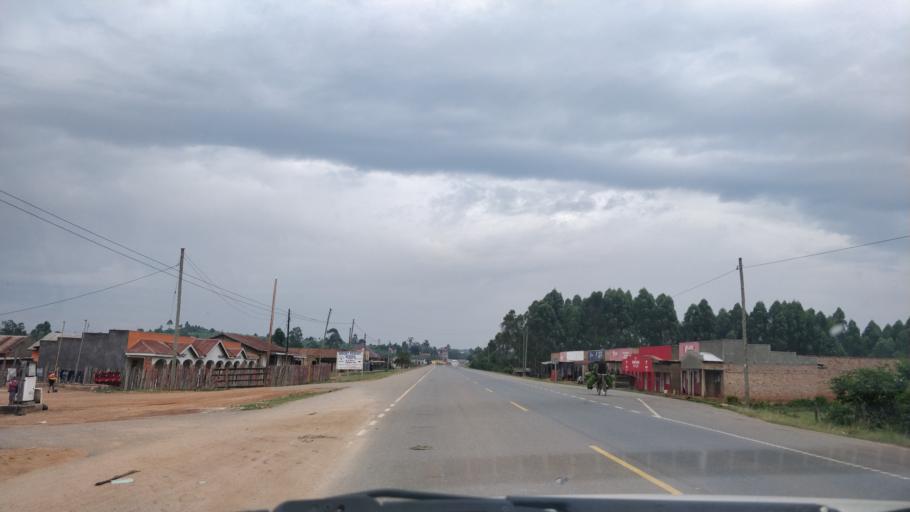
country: UG
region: Western Region
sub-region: Sheema District
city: Kibingo
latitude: -0.6634
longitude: 30.4514
